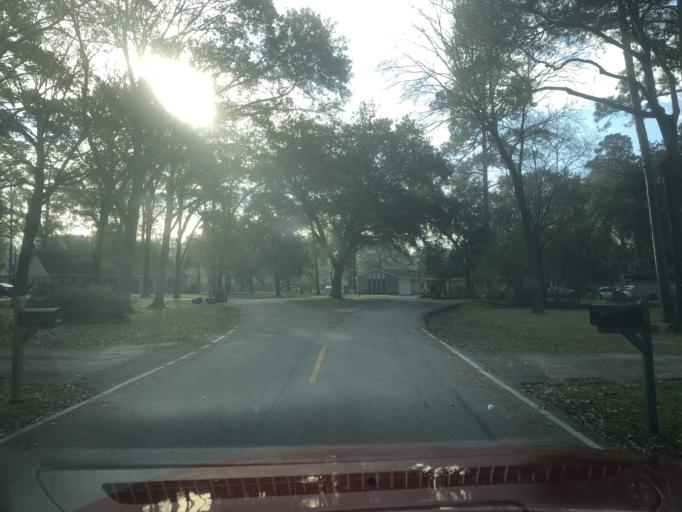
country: US
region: Texas
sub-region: Harris County
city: Spring
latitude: 30.0170
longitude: -95.4748
